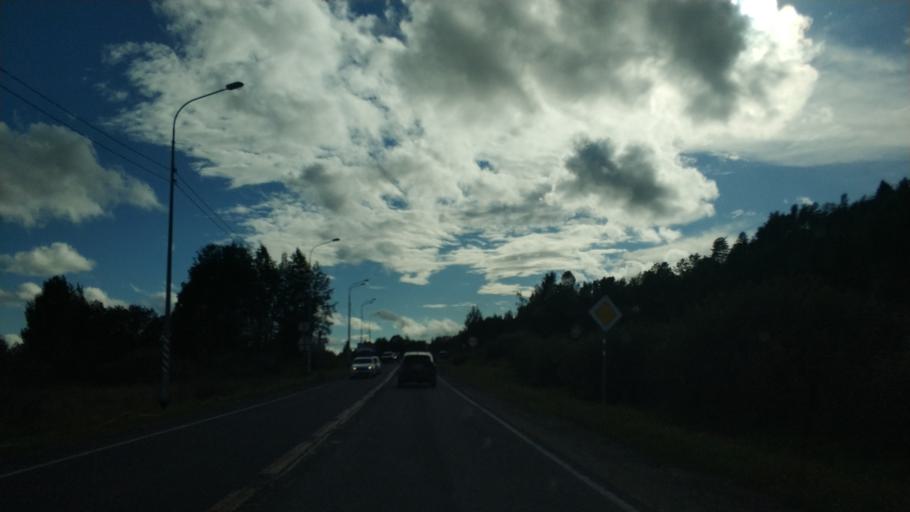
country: RU
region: Republic of Karelia
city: Lakhdenpokh'ya
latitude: 61.5562
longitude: 30.3245
